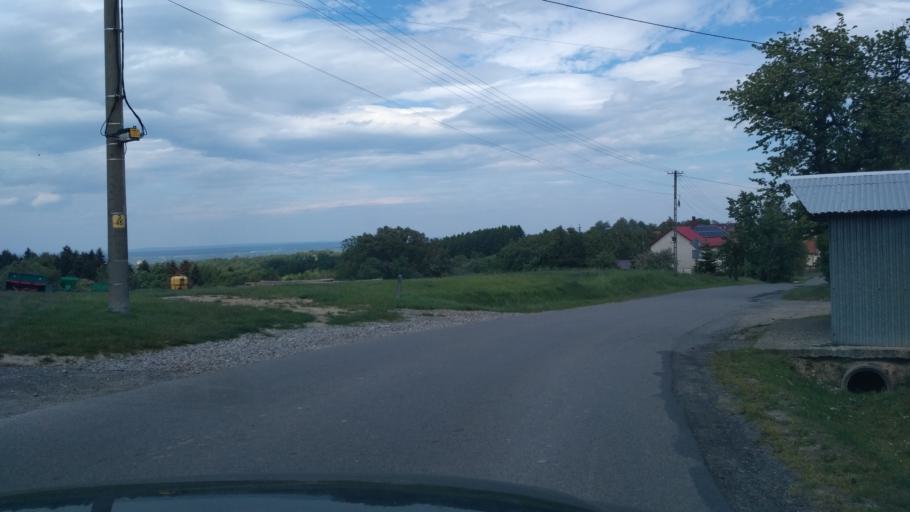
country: PL
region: Subcarpathian Voivodeship
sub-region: Powiat ropczycko-sedziszowski
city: Ropczyce
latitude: 50.0246
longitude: 21.6044
